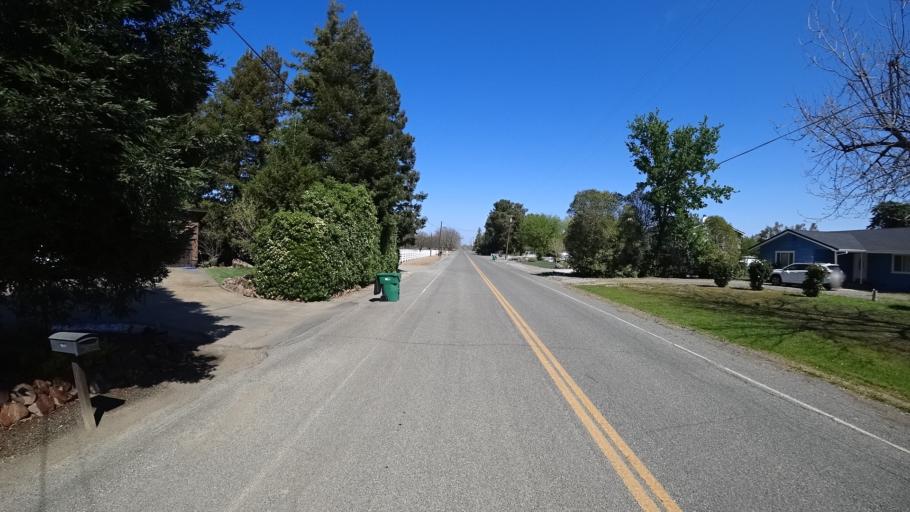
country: US
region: California
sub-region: Glenn County
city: Willows
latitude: 39.5350
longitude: -122.2075
